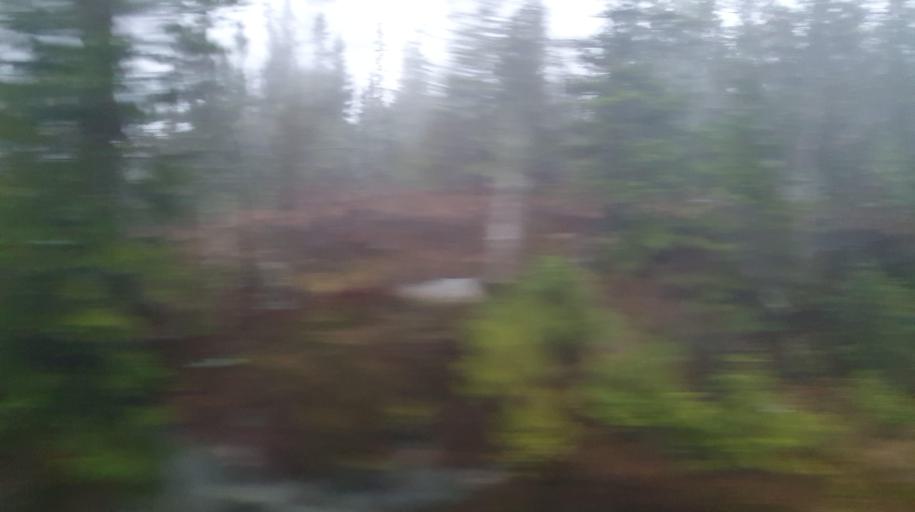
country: NO
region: Buskerud
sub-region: Krodsherad
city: Noresund
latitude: 60.2151
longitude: 9.5487
